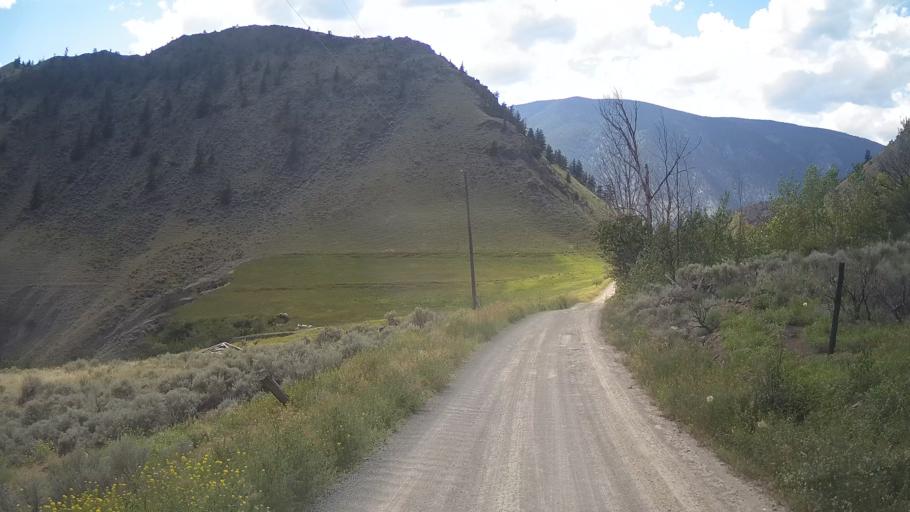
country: CA
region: British Columbia
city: Lillooet
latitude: 51.1981
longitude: -122.1044
